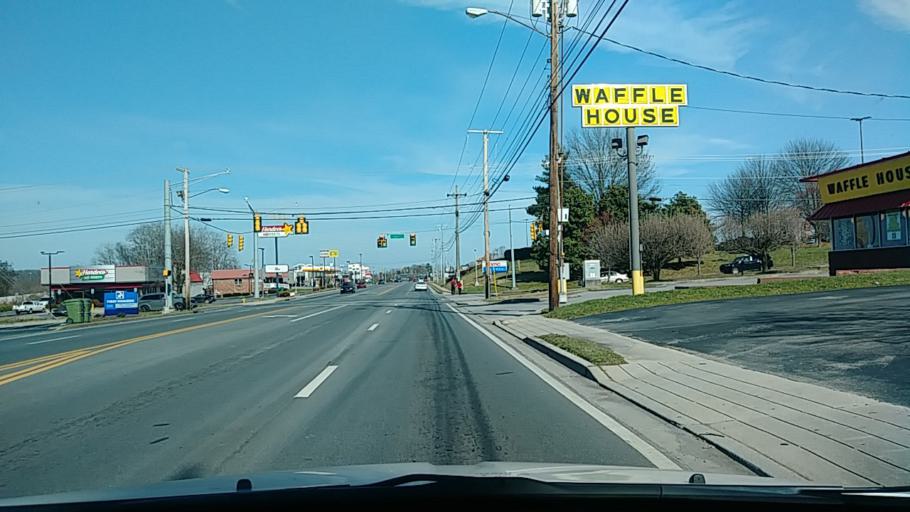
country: US
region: Tennessee
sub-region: Hamblen County
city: Morristown
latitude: 36.2212
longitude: -83.2652
